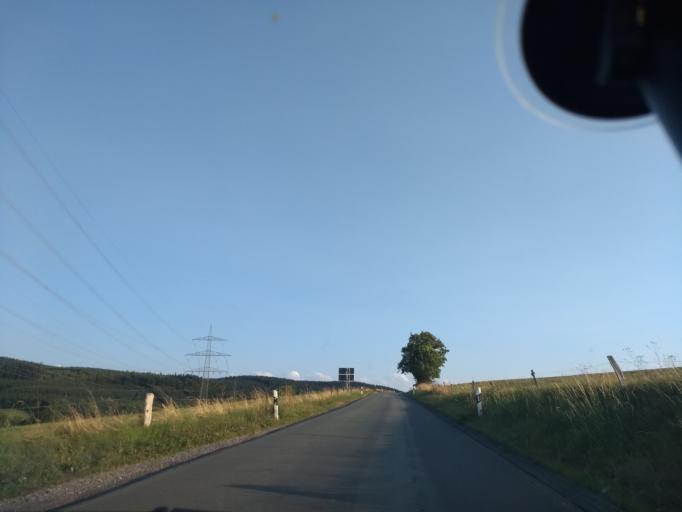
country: DE
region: North Rhine-Westphalia
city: Eslohe
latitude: 51.2792
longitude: 8.0815
